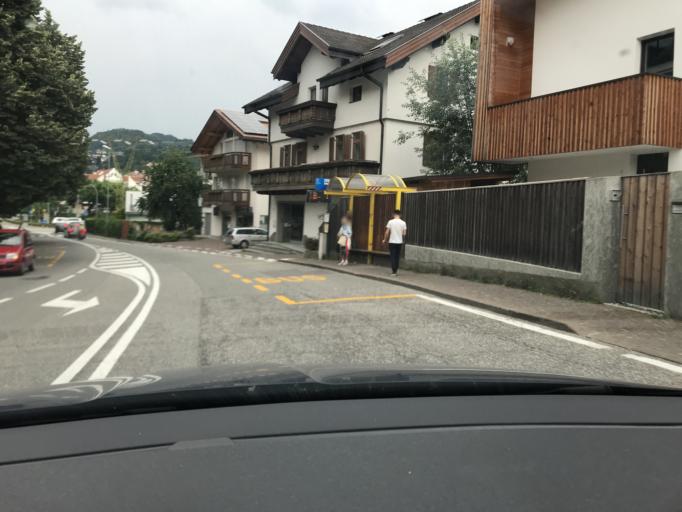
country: IT
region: Trentino-Alto Adige
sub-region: Bolzano
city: Bressanone
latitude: 46.7081
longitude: 11.6614
